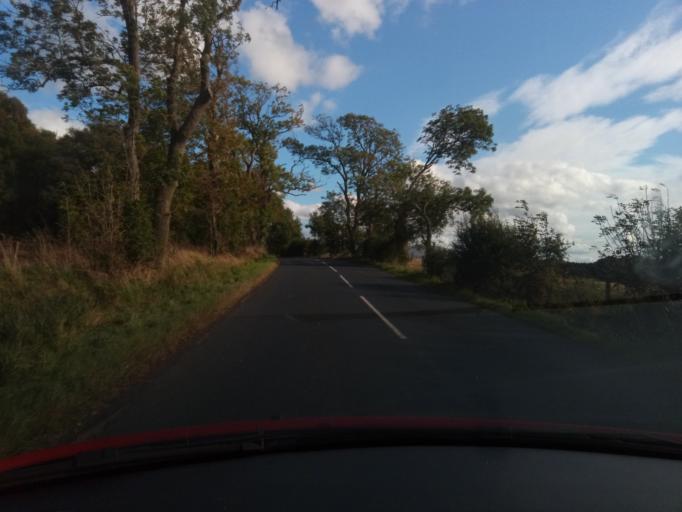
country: GB
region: Scotland
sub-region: The Scottish Borders
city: Kelso
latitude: 55.5662
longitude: -2.3520
